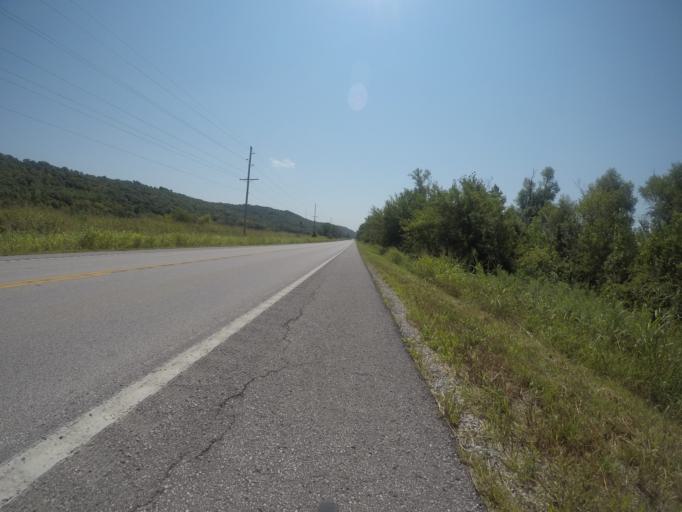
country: US
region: Kansas
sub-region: Atchison County
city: Atchison
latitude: 39.5054
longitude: -95.0109
